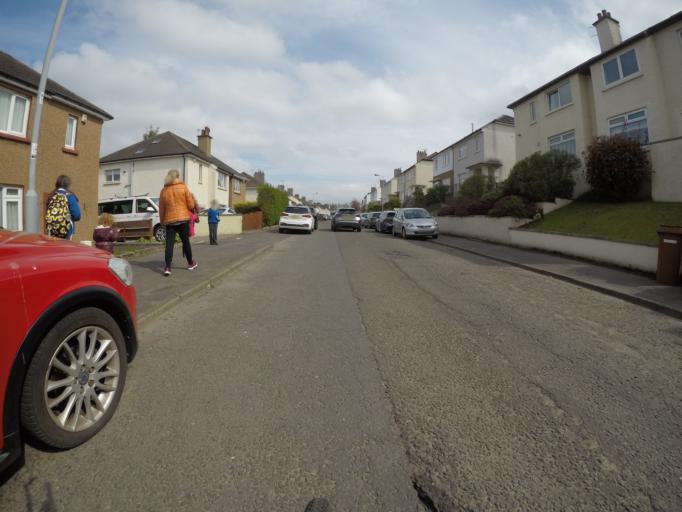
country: GB
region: Scotland
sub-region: East Renfrewshire
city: Giffnock
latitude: 55.8075
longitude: -4.2825
